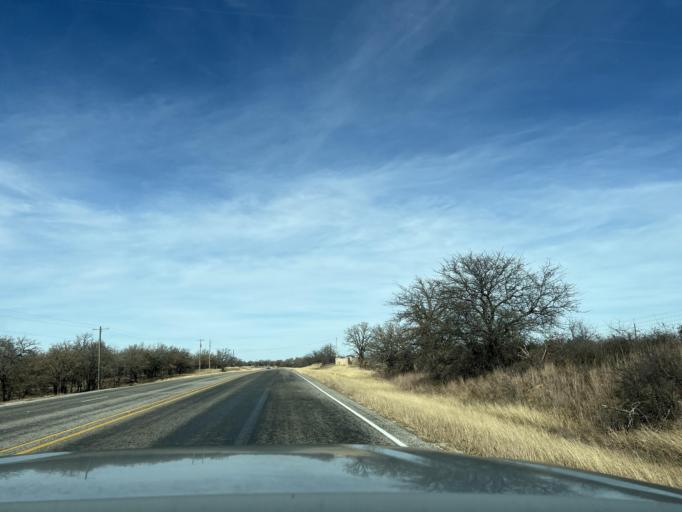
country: US
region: Texas
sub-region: Eastland County
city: Cisco
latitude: 32.4437
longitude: -98.9801
